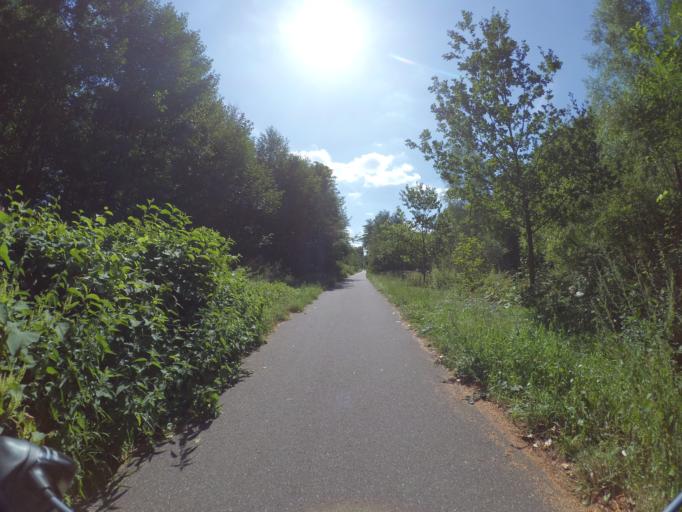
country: DE
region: Rheinland-Pfalz
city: Kenn
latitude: 49.7810
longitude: 6.7128
